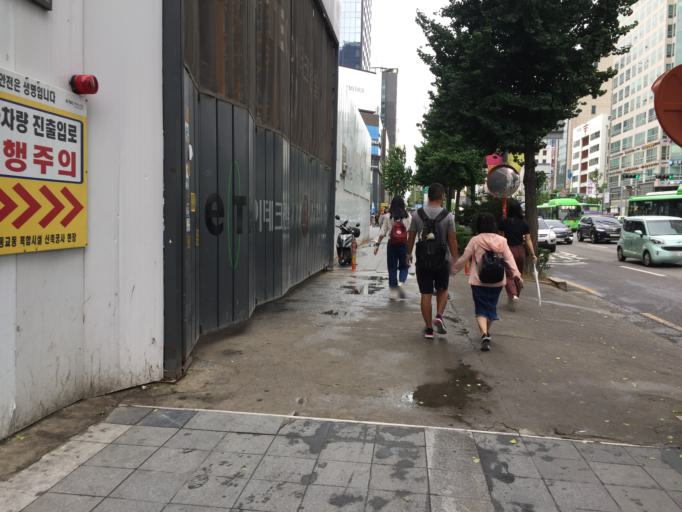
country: KR
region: Seoul
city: Seoul
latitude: 37.5560
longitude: 126.9219
